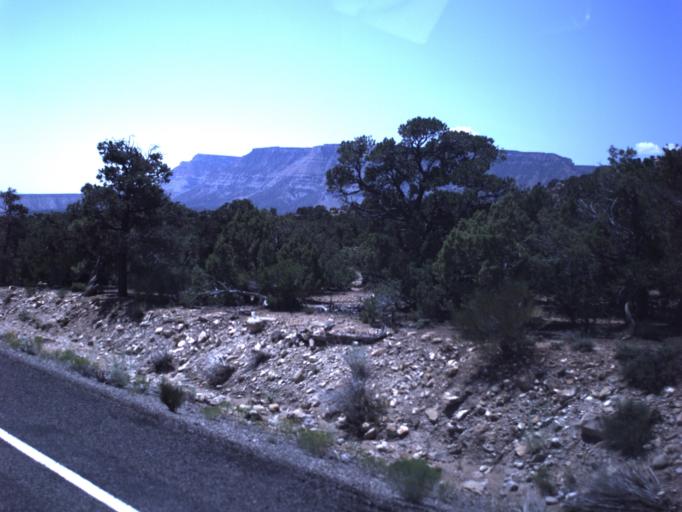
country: US
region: Utah
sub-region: Emery County
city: Orangeville
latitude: 39.3023
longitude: -111.1182
